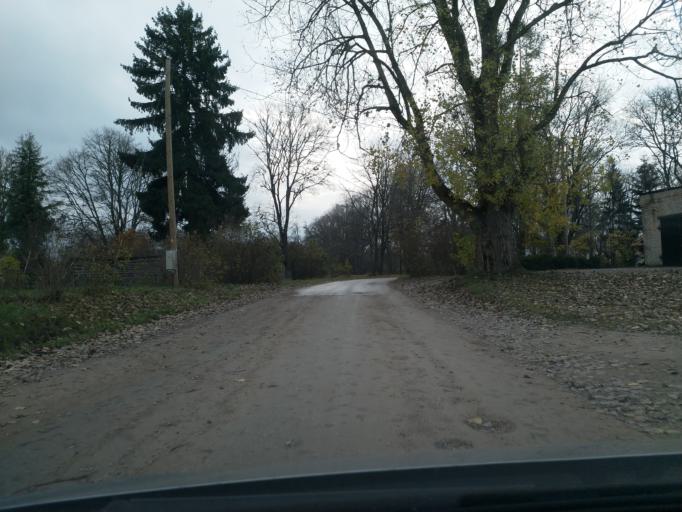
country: LV
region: Kuldigas Rajons
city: Kuldiga
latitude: 56.9824
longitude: 21.9740
